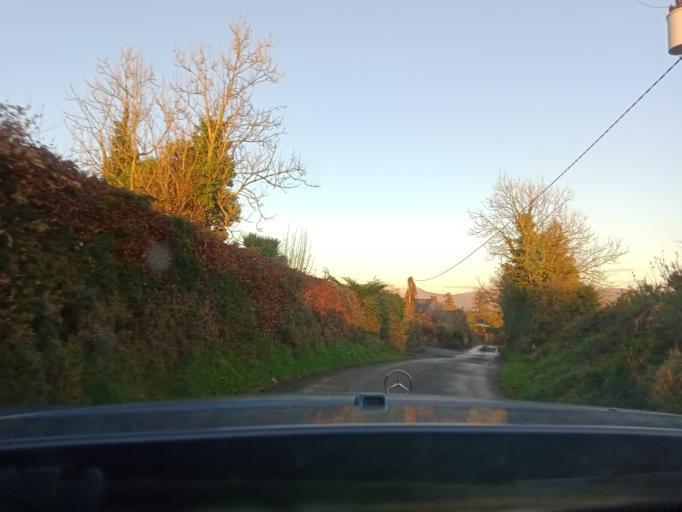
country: IE
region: Leinster
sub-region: Kilkenny
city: Graiguenamanagh
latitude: 52.4815
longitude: -6.9383
